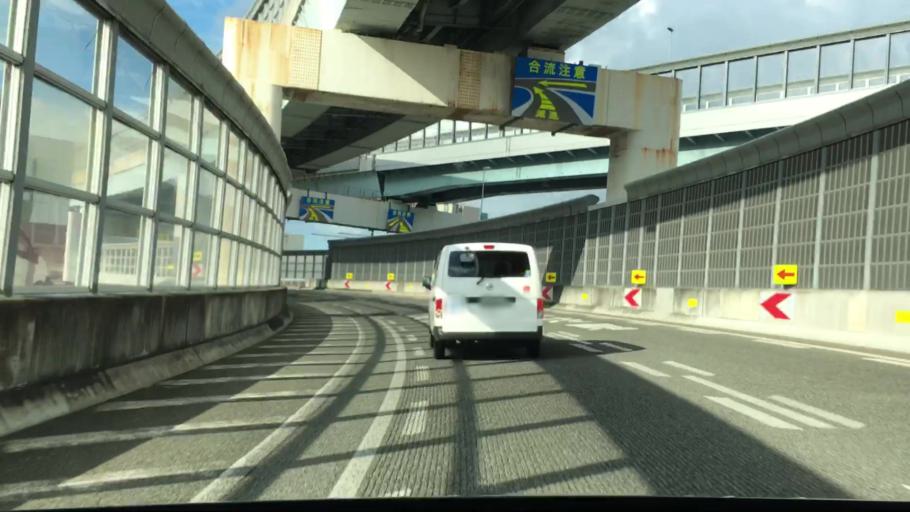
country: JP
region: Fukuoka
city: Fukuoka-shi
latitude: 33.5694
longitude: 130.3167
